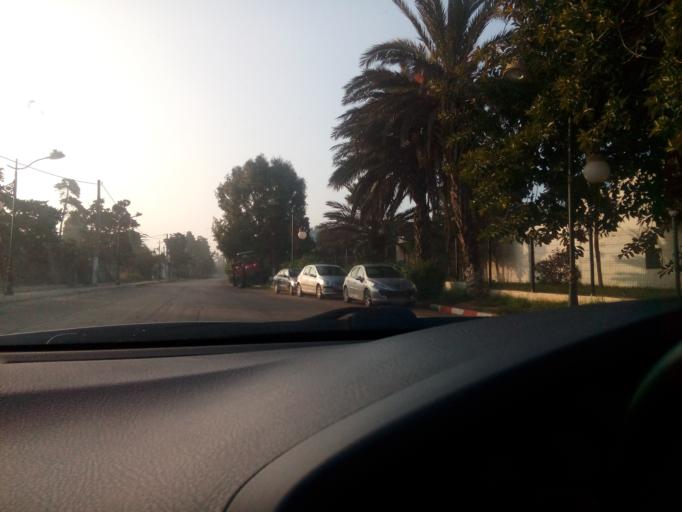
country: DZ
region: Oran
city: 'Ain el Turk
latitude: 35.7045
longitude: -0.8926
